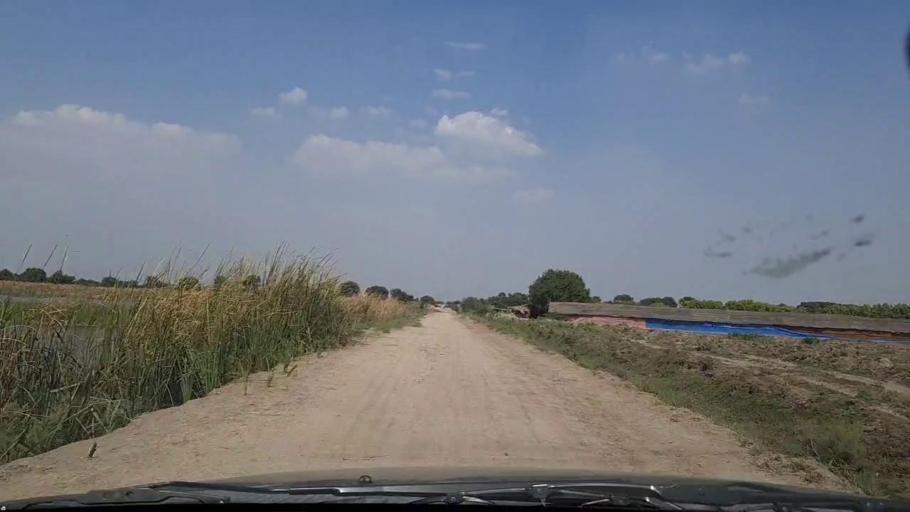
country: PK
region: Sindh
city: Mirpur Batoro
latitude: 24.6240
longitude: 68.2417
